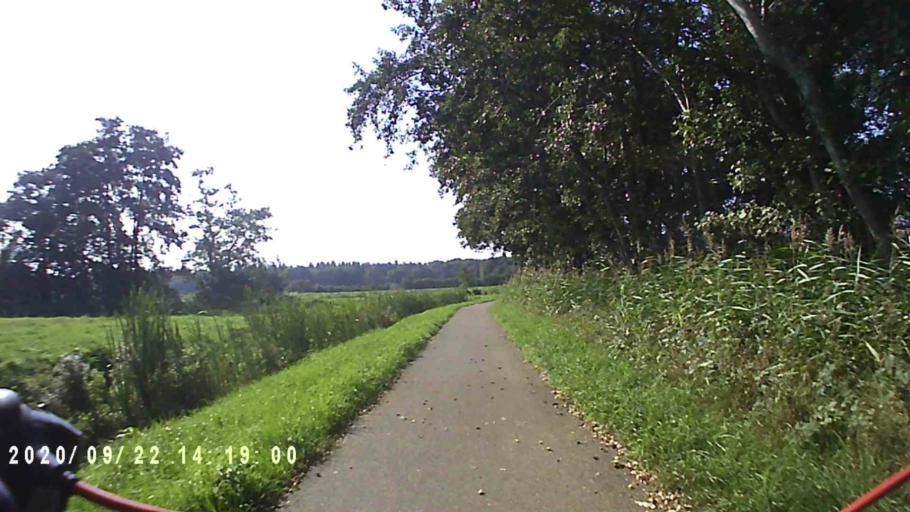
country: NL
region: Groningen
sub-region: Gemeente Leek
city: Leek
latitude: 53.0654
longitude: 6.4138
